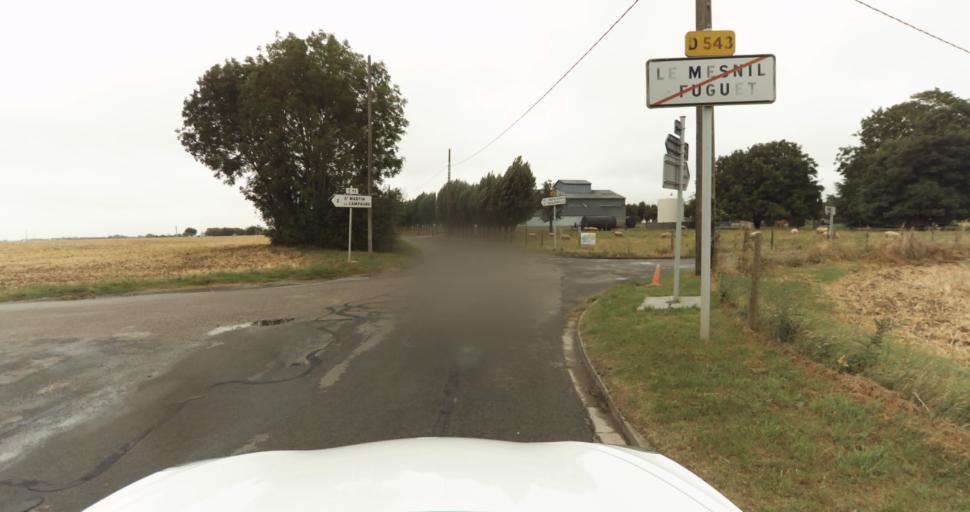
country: FR
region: Haute-Normandie
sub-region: Departement de l'Eure
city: Aviron
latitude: 49.0705
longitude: 1.0969
